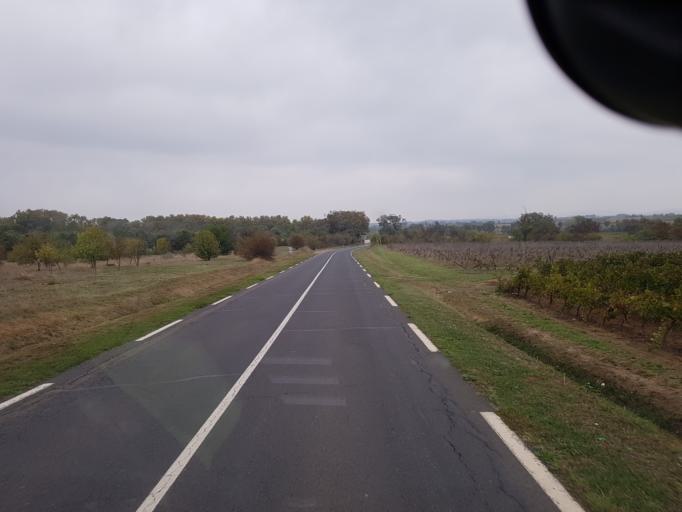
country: FR
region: Languedoc-Roussillon
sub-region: Departement de l'Herault
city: Pinet
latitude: 43.4006
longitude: 3.5391
